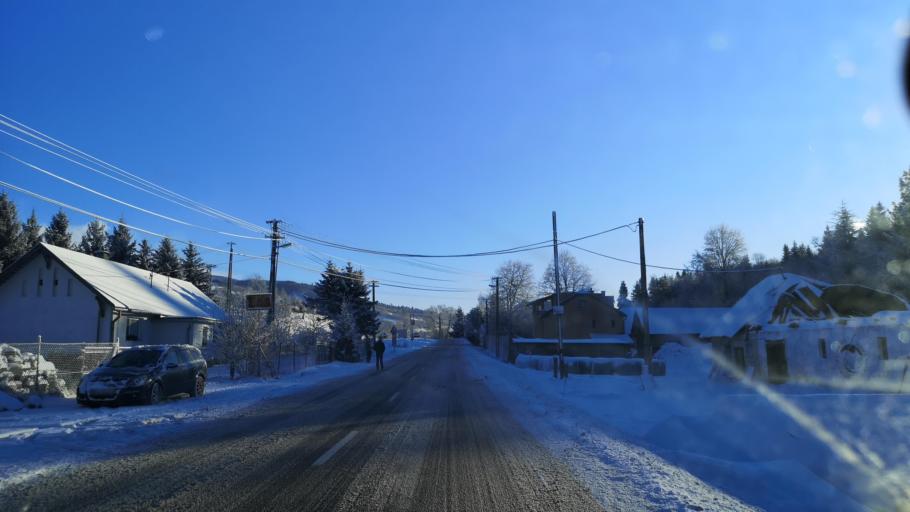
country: SK
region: Banskobystricky
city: Tisovec
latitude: 48.8515
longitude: 20.0096
